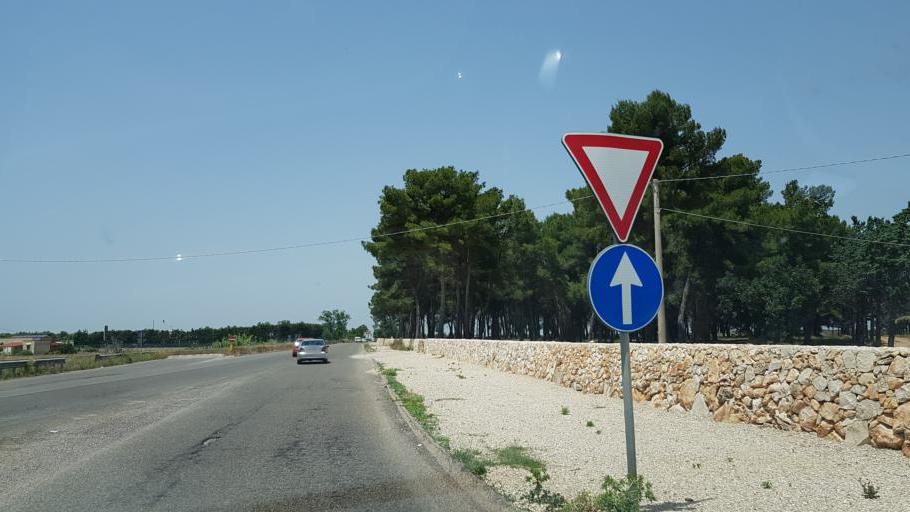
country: IT
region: Apulia
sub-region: Provincia di Lecce
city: Porto Cesareo
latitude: 40.2680
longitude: 17.9105
